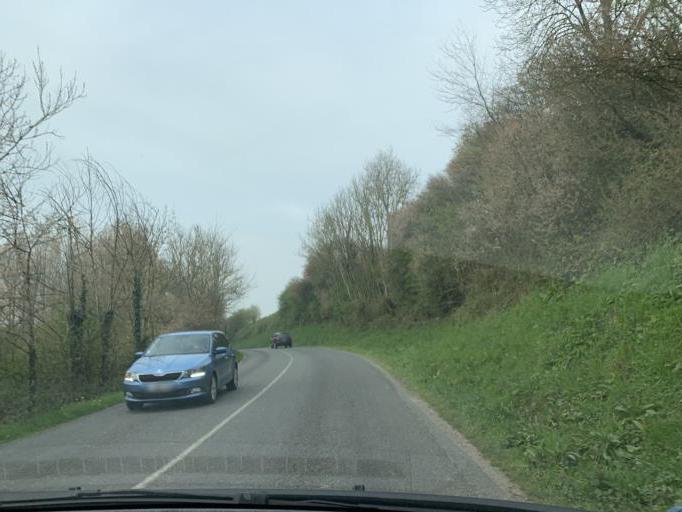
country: FR
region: Nord-Pas-de-Calais
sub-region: Departement du Pas-de-Calais
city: Montreuil
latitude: 50.4813
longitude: 1.7746
